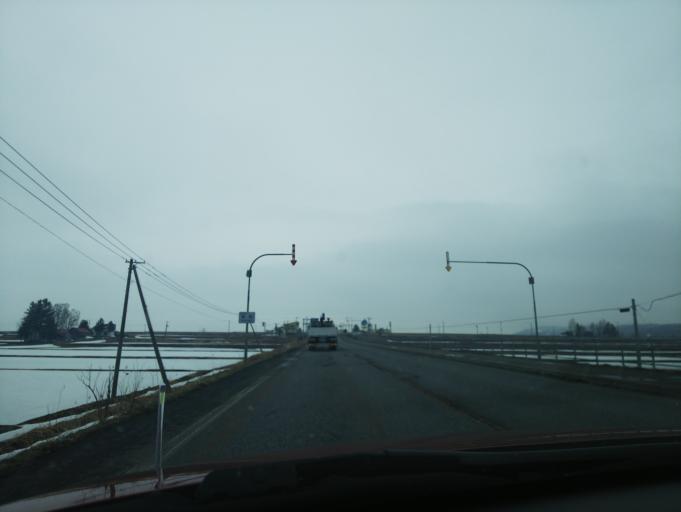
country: JP
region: Hokkaido
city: Nayoro
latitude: 44.0682
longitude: 142.3964
